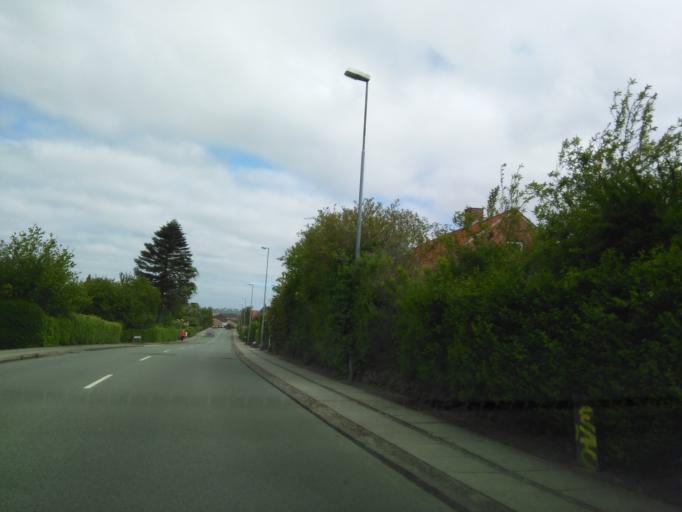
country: DK
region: Central Jutland
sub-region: Arhus Kommune
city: Stavtrup
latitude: 56.1182
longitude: 10.1723
